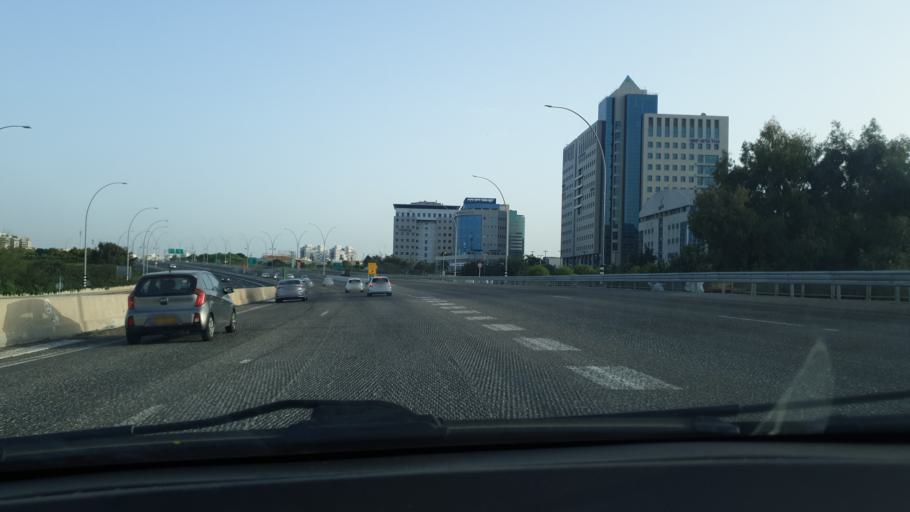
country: IL
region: Central District
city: Ra'anana
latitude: 32.1988
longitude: 34.8847
